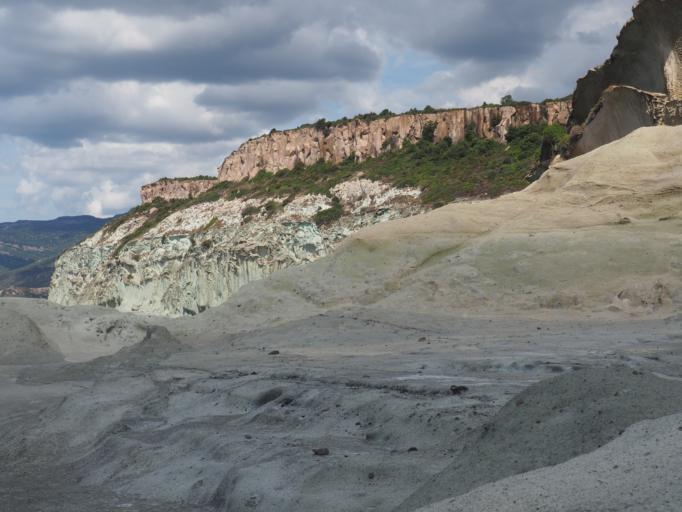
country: IT
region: Sardinia
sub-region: Provincia di Oristano
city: Bosa
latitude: 40.2945
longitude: 8.4692
